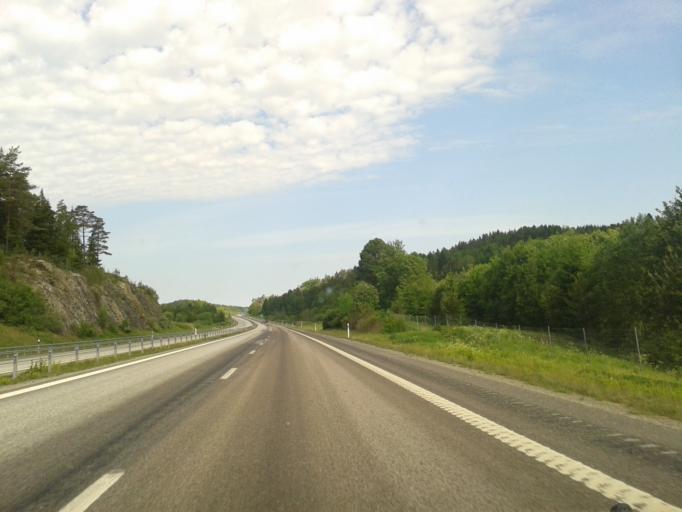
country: SE
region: Vaestra Goetaland
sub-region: Lysekils Kommun
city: Brastad
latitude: 58.5504
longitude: 11.5077
